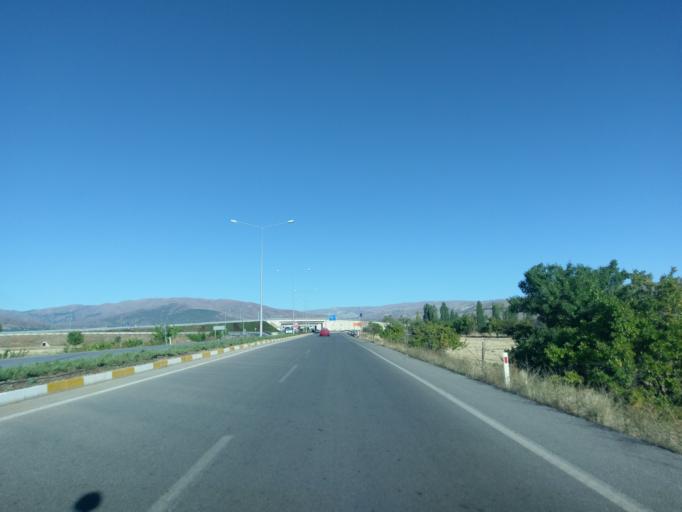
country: TR
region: Erzincan
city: Catalarmut
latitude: 39.7873
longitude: 39.3983
